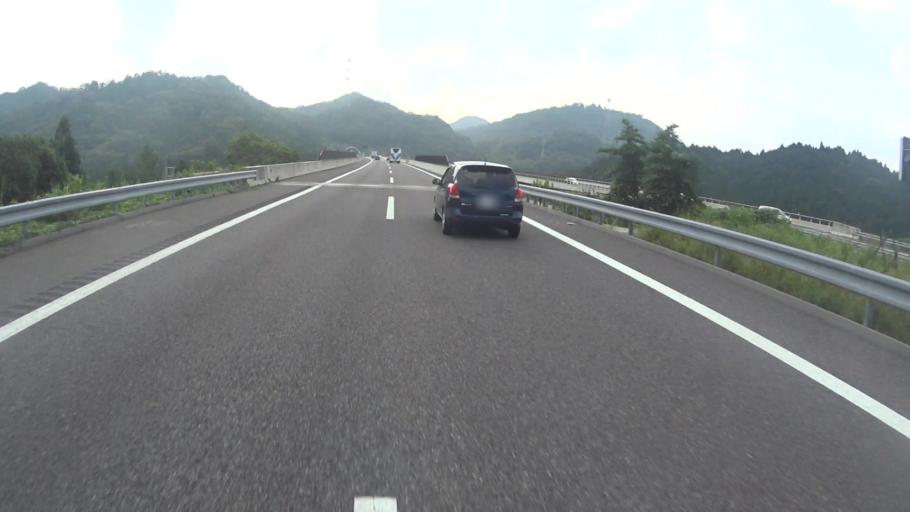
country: JP
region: Shiga Prefecture
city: Minakuchicho-matoba
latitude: 34.9186
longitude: 136.1428
